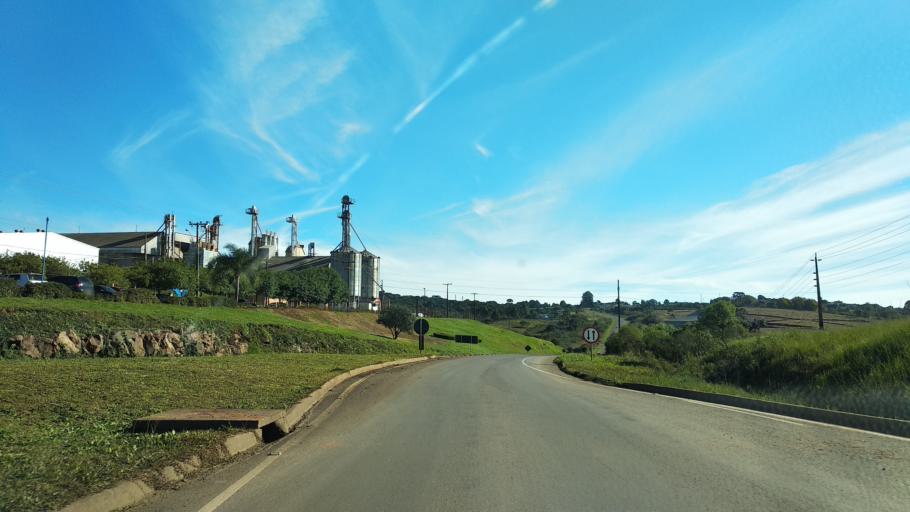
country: BR
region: Santa Catarina
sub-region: Campos Novos
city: Campos Novos
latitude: -27.4085
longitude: -51.2158
